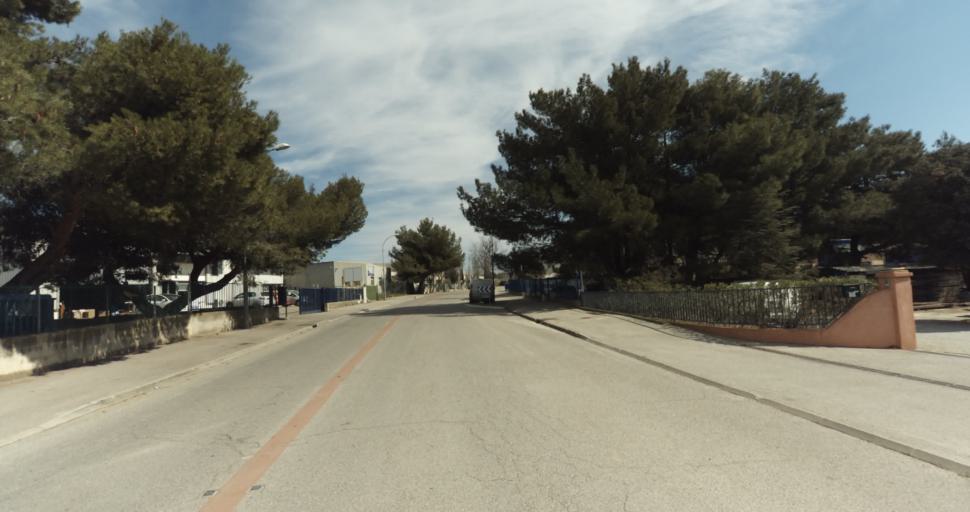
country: FR
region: Provence-Alpes-Cote d'Azur
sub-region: Departement des Bouches-du-Rhone
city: Lambesc
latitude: 43.6474
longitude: 5.2582
